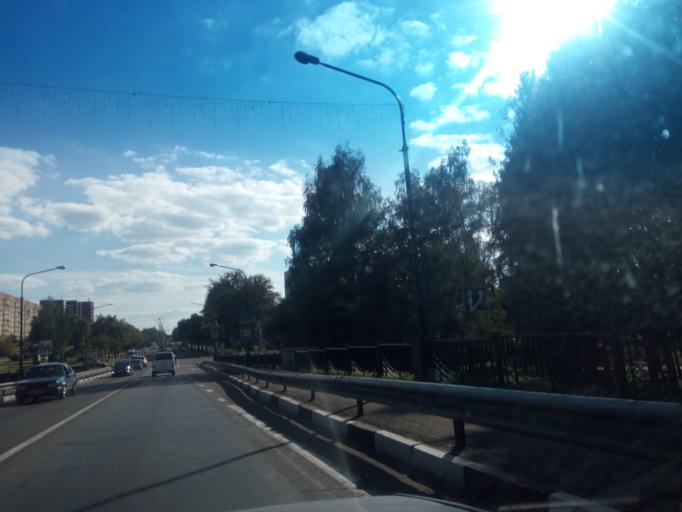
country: BY
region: Vitebsk
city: Navapolatsk
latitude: 55.5362
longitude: 28.6633
